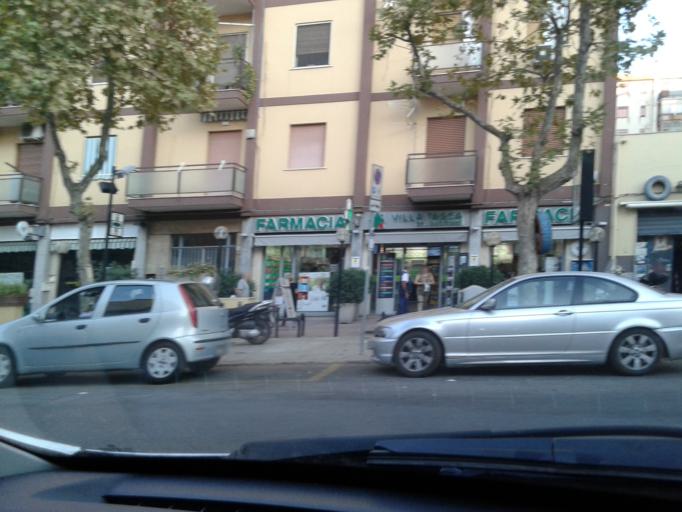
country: IT
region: Sicily
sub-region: Palermo
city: Palermo
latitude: 38.0999
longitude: 13.3369
